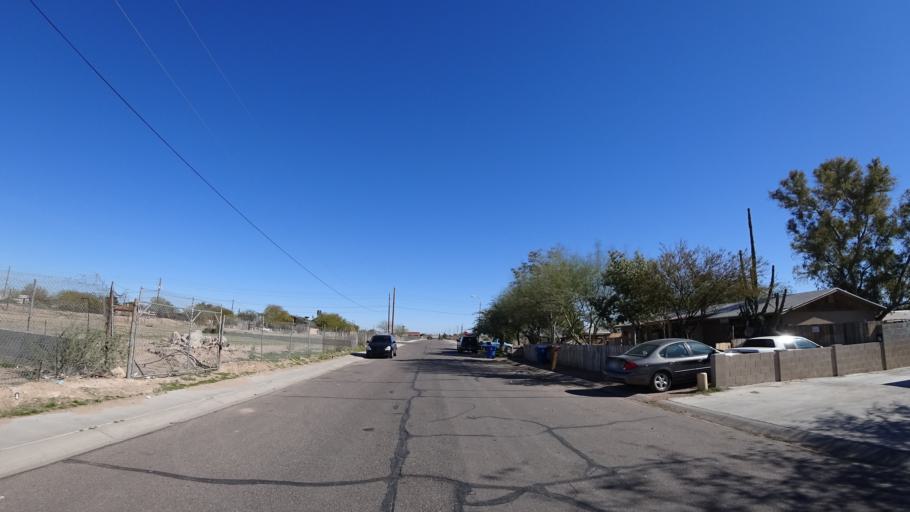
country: US
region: Arizona
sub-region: Maricopa County
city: Avondale
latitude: 33.4143
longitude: -112.3287
